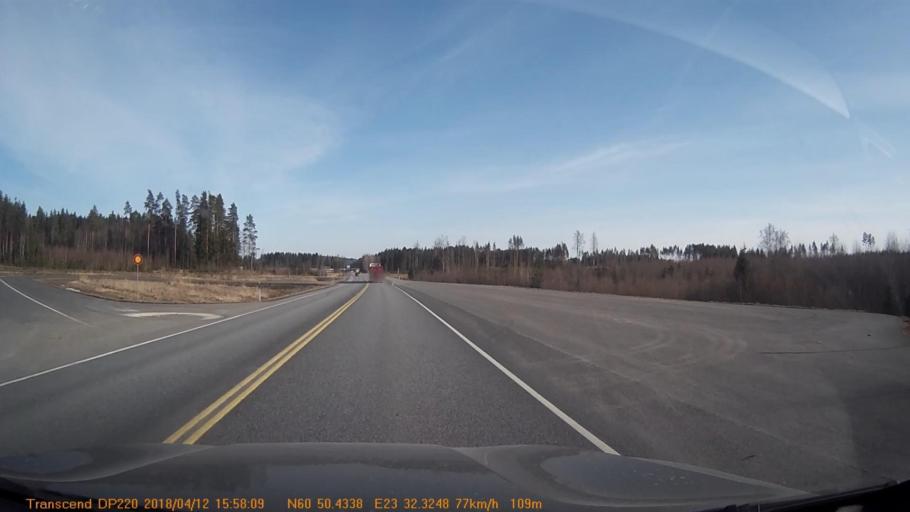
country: FI
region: Haeme
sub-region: Forssa
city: Jokioinen
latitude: 60.8400
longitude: 23.5399
